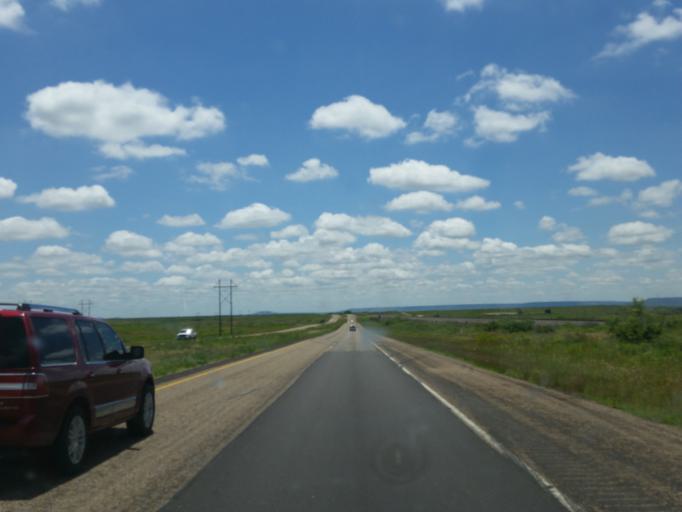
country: US
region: Texas
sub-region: Garza County
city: Post
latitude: 33.1176
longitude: -101.2783
